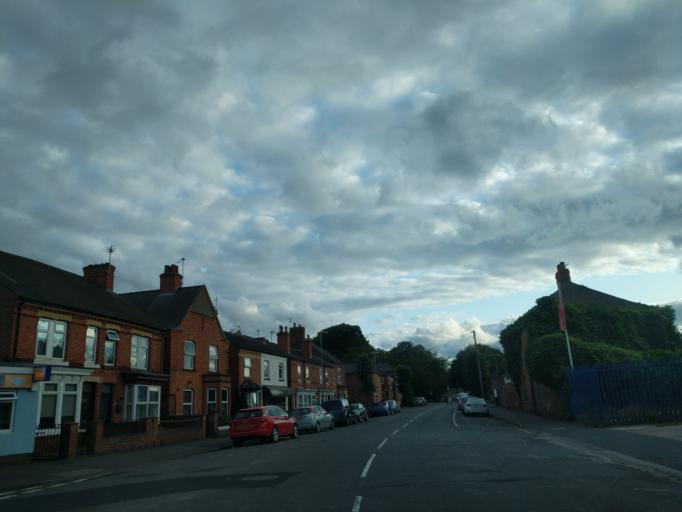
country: GB
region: England
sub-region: Nottinghamshire
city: Newark on Trent
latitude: 53.0796
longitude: -0.8026
